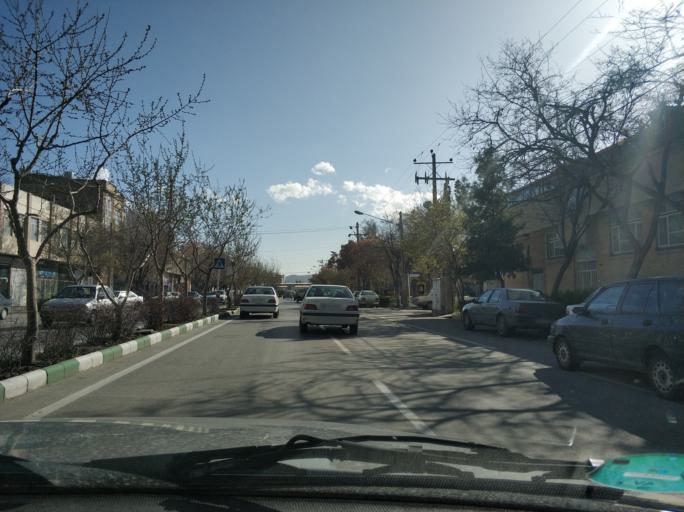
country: IR
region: Razavi Khorasan
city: Mashhad
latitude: 36.3127
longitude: 59.6252
